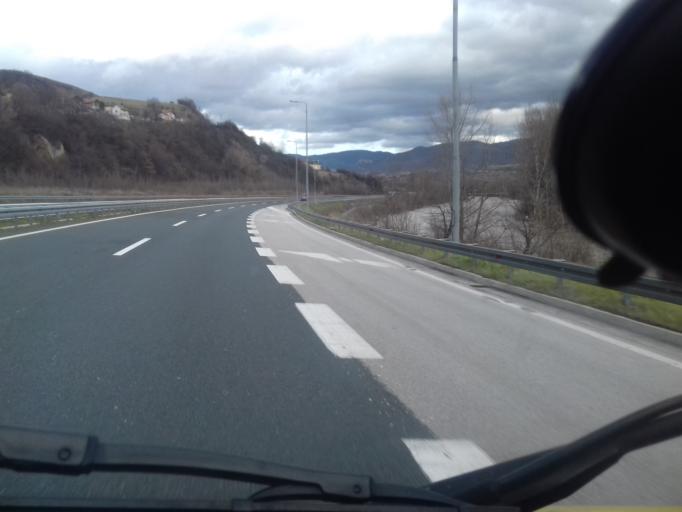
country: BA
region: Federation of Bosnia and Herzegovina
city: Kakanj
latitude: 44.1000
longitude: 18.1069
